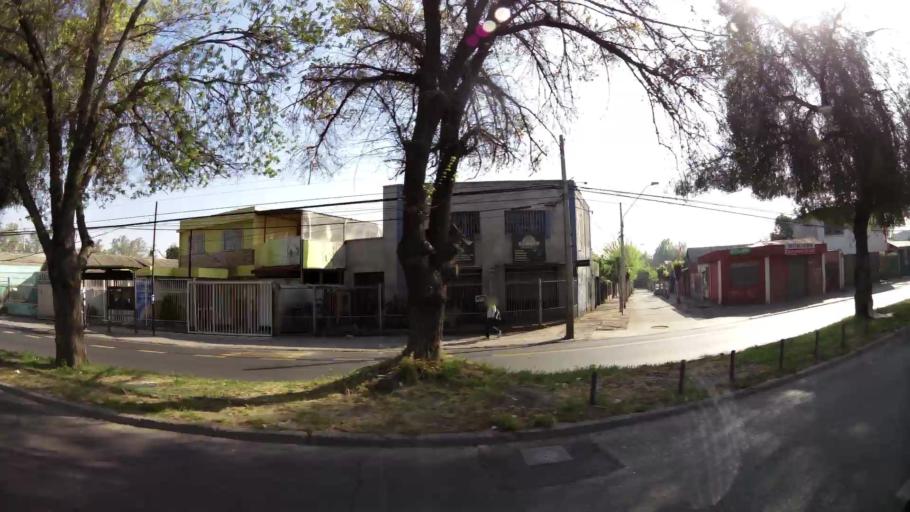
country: CL
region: Santiago Metropolitan
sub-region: Provincia de Santiago
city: Lo Prado
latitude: -33.3766
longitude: -70.6845
